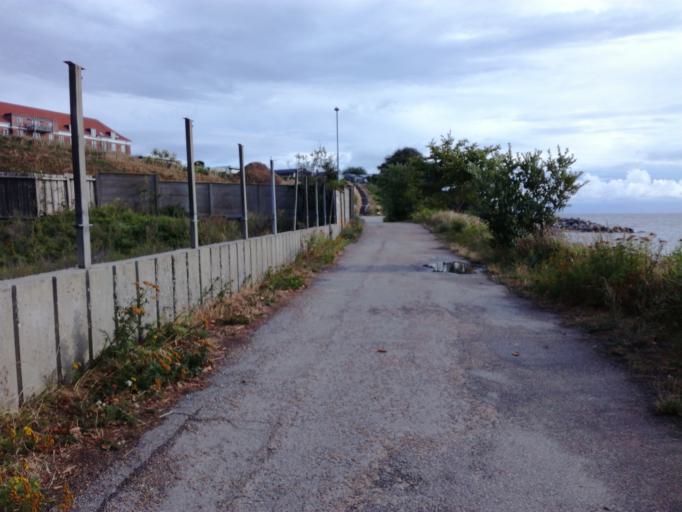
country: DK
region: South Denmark
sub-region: Fredericia Kommune
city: Fredericia
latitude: 55.5706
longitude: 9.7713
